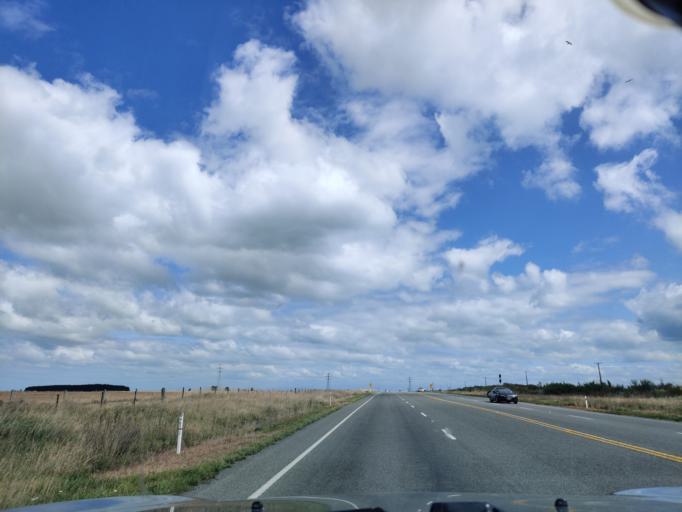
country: NZ
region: Canterbury
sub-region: Timaru District
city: Pleasant Point
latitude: -44.0785
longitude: 171.3512
